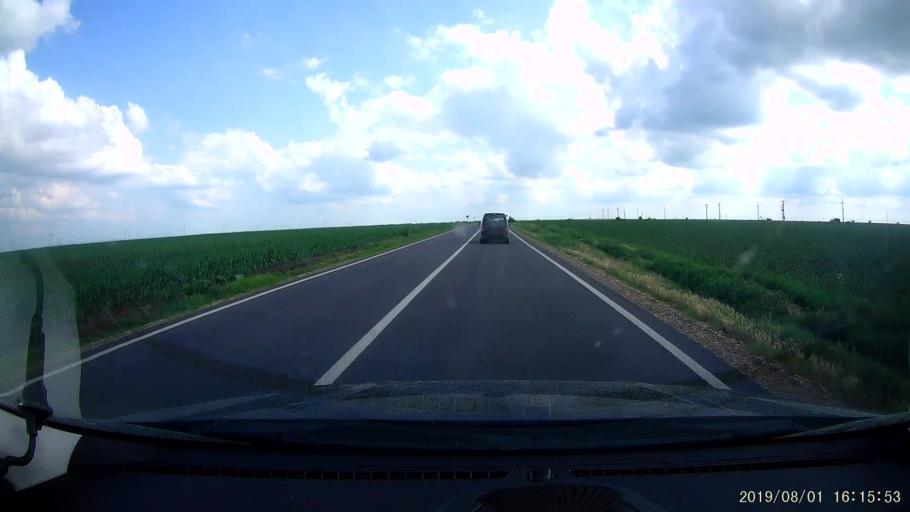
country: RO
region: Calarasi
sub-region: Comuna Stefan Voda
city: Stefan Voda
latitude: 44.3302
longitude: 27.3597
